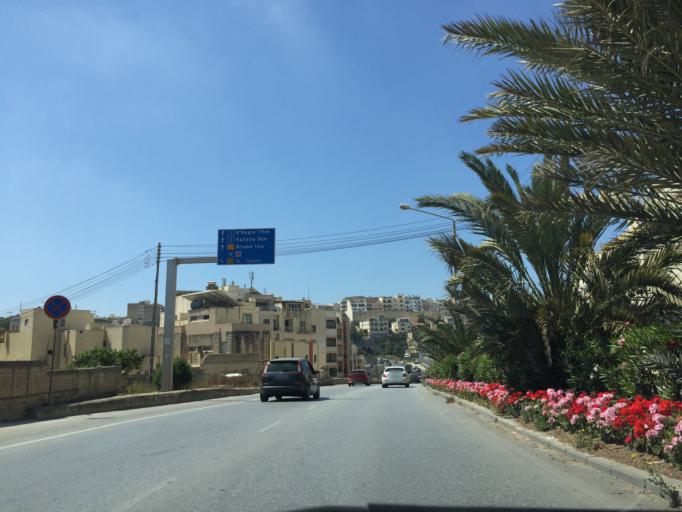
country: MT
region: Saint Julian
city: San Giljan
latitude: 35.9184
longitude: 14.4867
